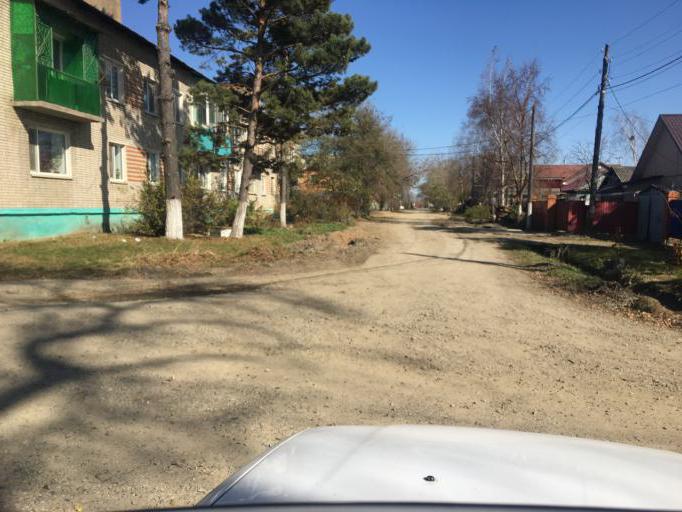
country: RU
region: Primorskiy
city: Dal'nerechensk
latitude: 45.9305
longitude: 133.7438
